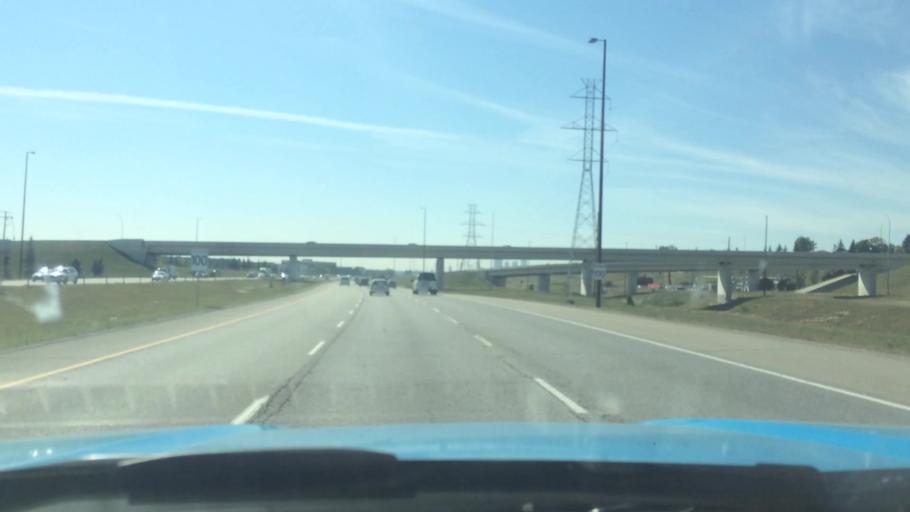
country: CA
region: Alberta
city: Calgary
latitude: 51.1280
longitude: -114.0471
